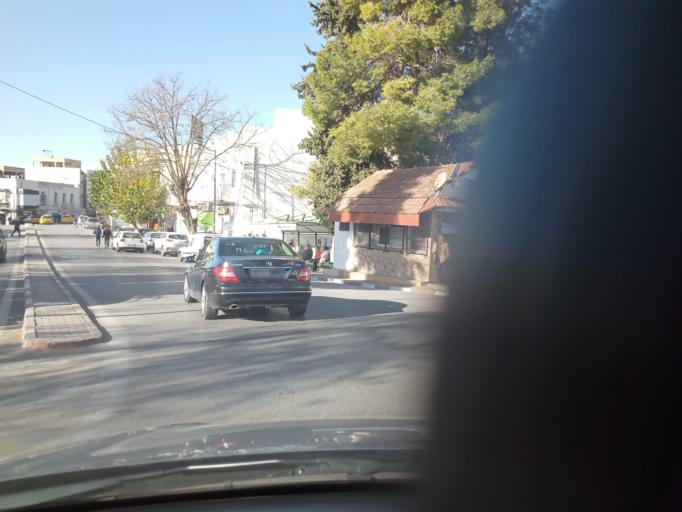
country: TN
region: Kef
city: El Kef
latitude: 36.1802
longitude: 8.7111
